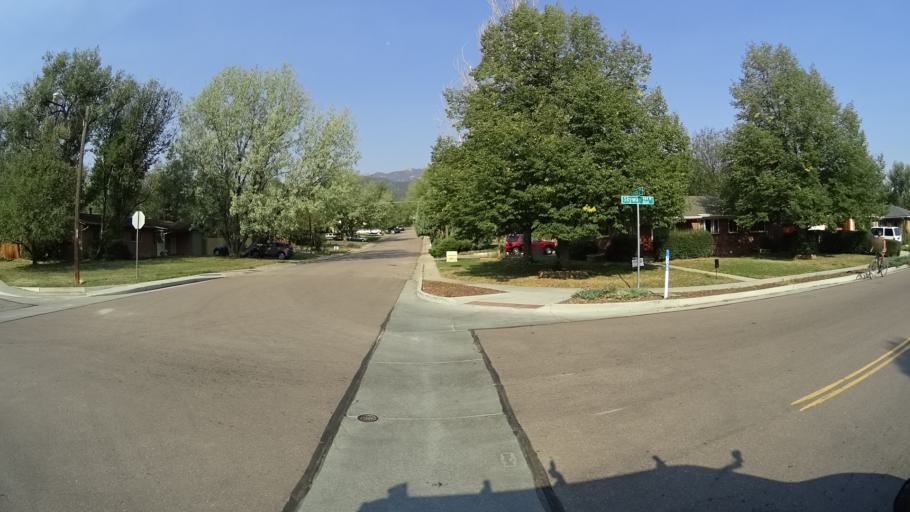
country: US
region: Colorado
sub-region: El Paso County
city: Colorado Springs
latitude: 38.8075
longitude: -104.8460
